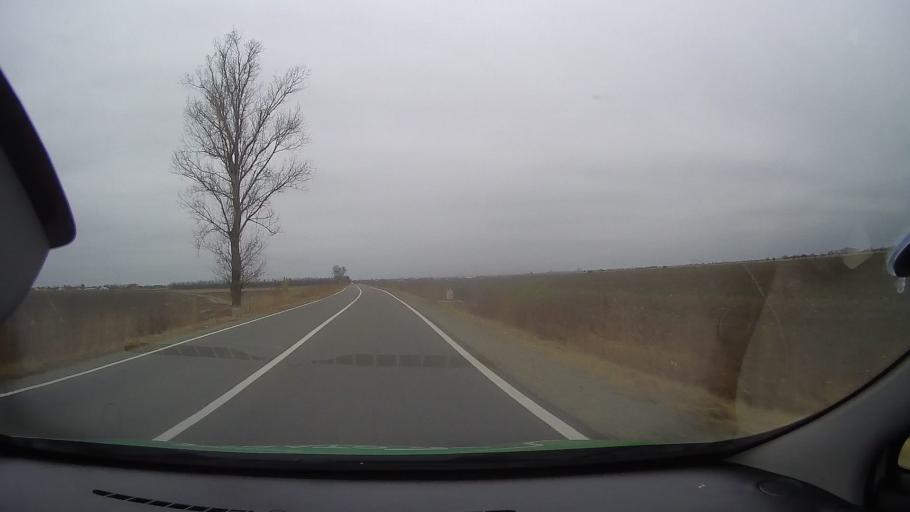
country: RO
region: Ialomita
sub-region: Comuna Slobozia
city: Slobozia
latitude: 44.6166
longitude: 27.3870
